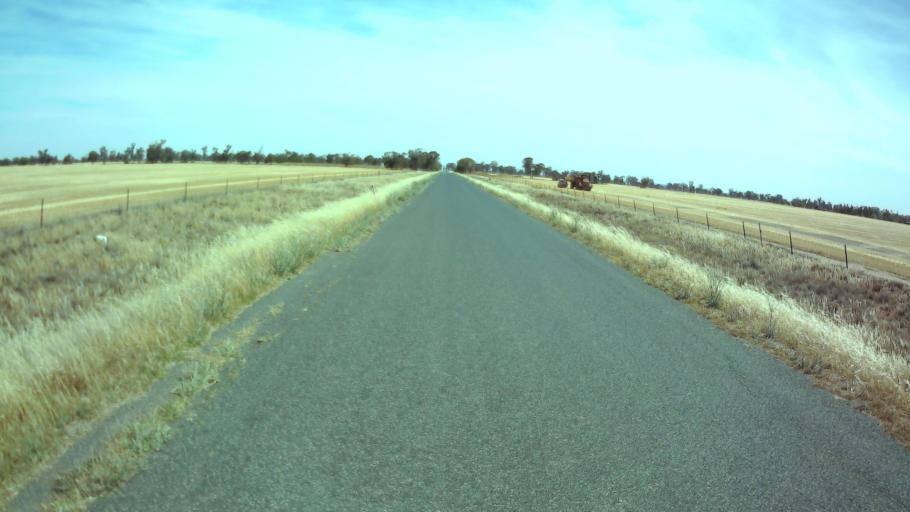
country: AU
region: New South Wales
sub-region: Weddin
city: Grenfell
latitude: -33.9891
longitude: 147.7764
